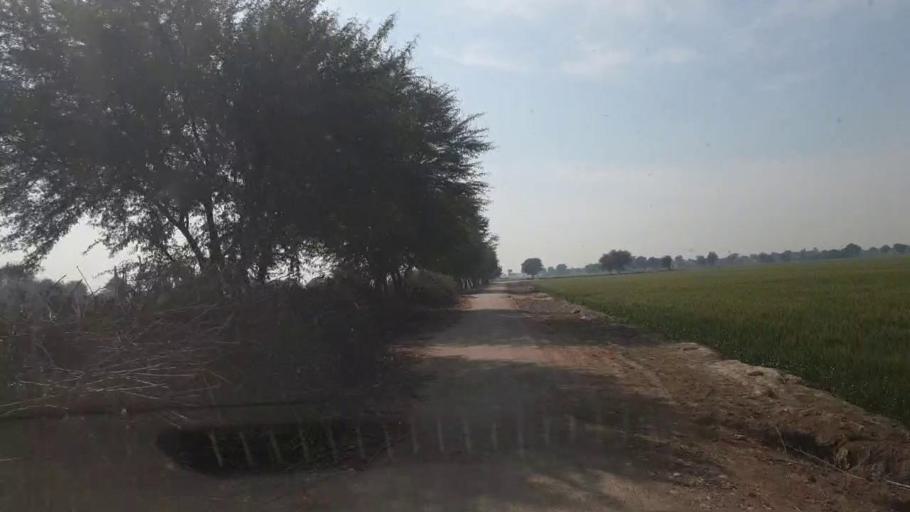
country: PK
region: Sindh
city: Nawabshah
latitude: 26.1646
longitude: 68.4973
